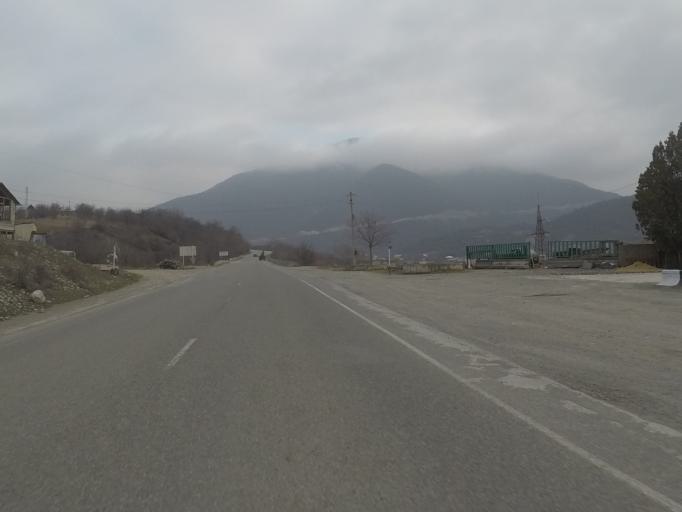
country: GE
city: Zhinvali
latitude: 42.1093
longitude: 44.7737
